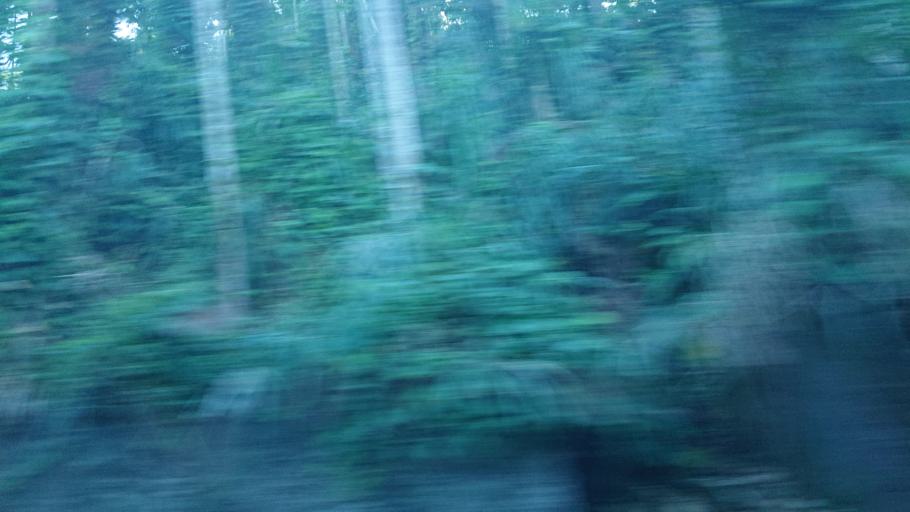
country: TW
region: Taiwan
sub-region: Chiayi
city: Jiayi Shi
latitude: 23.5188
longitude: 120.6258
